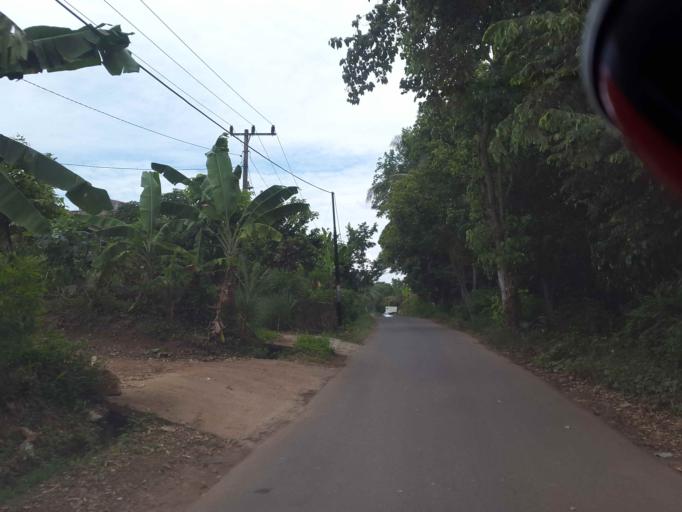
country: ID
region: Lampung
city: Kedaton
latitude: -5.3504
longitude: 105.2281
